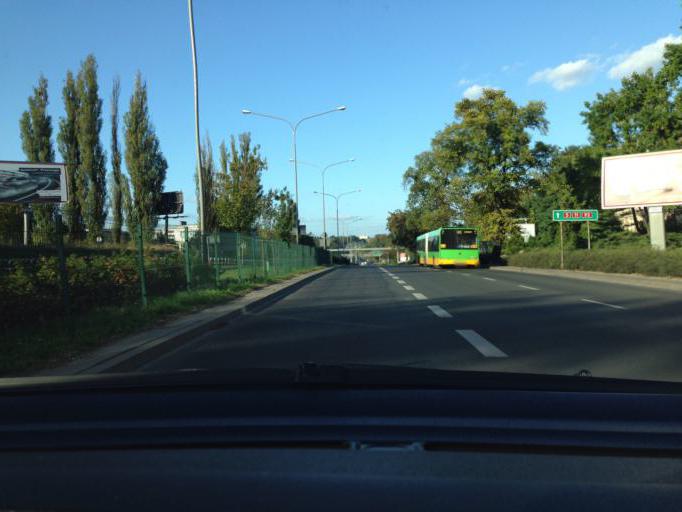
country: PL
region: Greater Poland Voivodeship
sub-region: Poznan
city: Poznan
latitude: 52.4163
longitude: 16.8921
